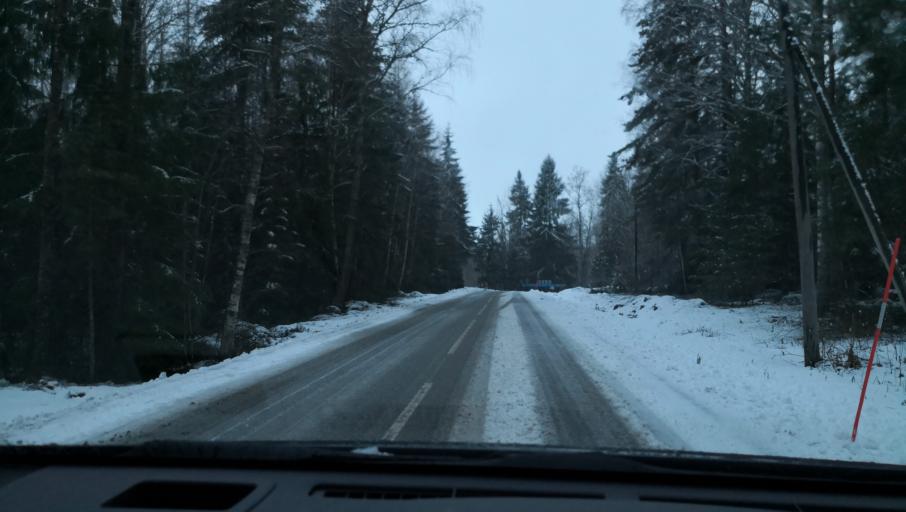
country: SE
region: Vaestmanland
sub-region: Kopings Kommun
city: Kolsva
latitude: 59.5672
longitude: 15.7824
